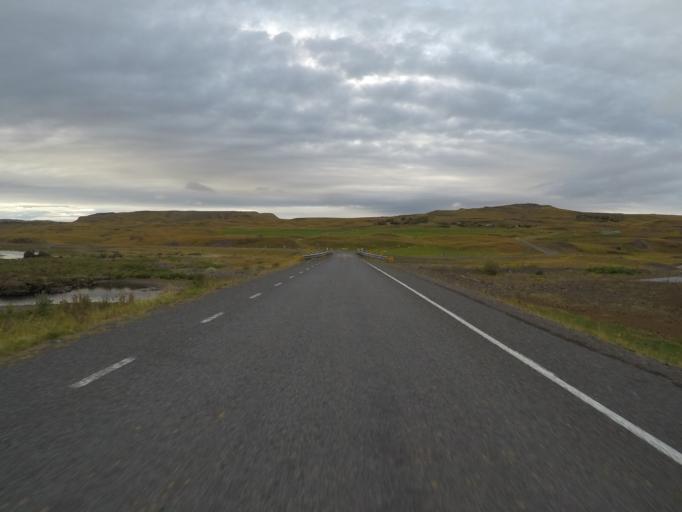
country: IS
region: South
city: Vestmannaeyjar
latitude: 64.0638
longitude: -20.1087
